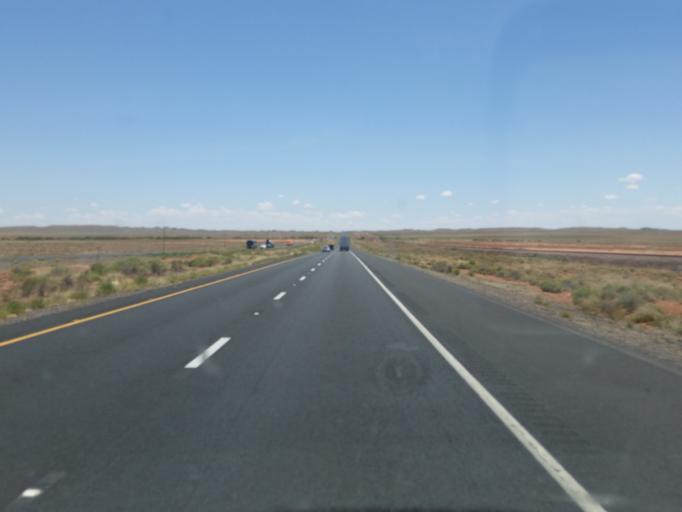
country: US
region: Arizona
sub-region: Coconino County
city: LeChee
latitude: 35.0554
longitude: -110.7949
